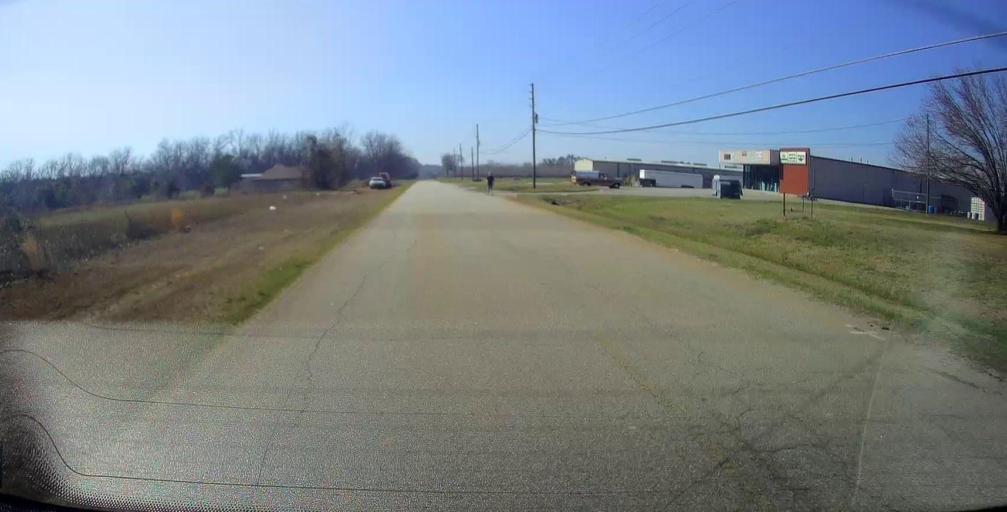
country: US
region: Georgia
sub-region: Houston County
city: Perry
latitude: 32.4657
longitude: -83.7499
